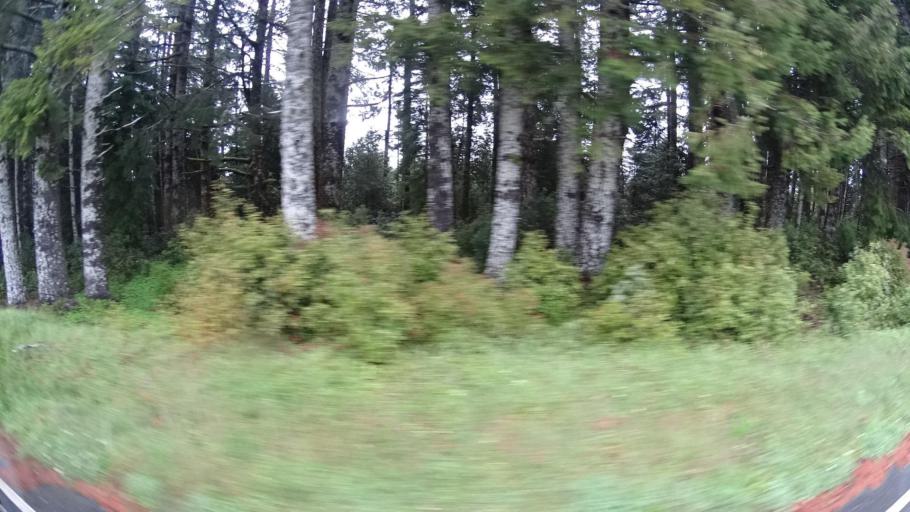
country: US
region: California
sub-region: Humboldt County
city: Westhaven-Moonstone
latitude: 41.1918
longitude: -123.9367
